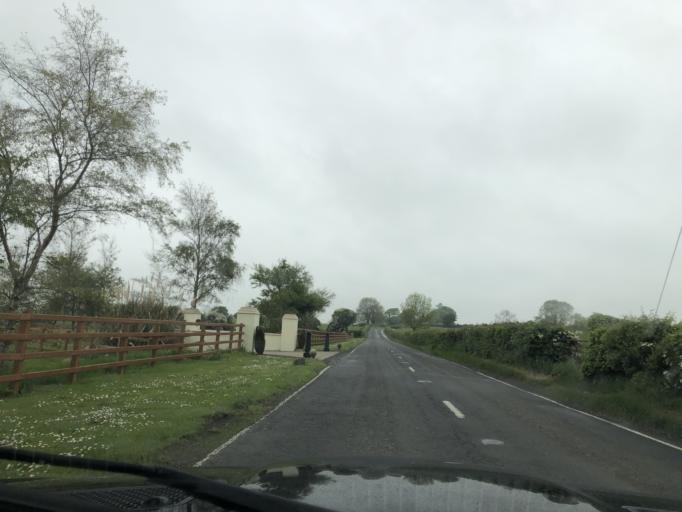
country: GB
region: Northern Ireland
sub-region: Down District
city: Portaferry
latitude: 54.3584
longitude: -5.5748
